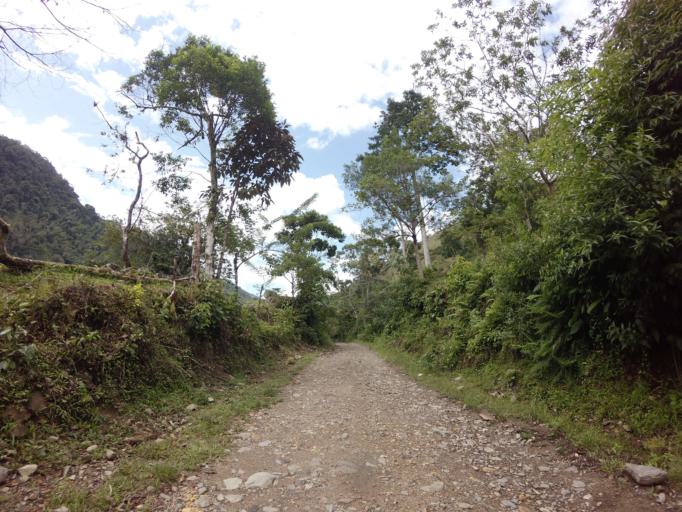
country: CO
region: Antioquia
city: Narino
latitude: 5.5296
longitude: -75.1579
